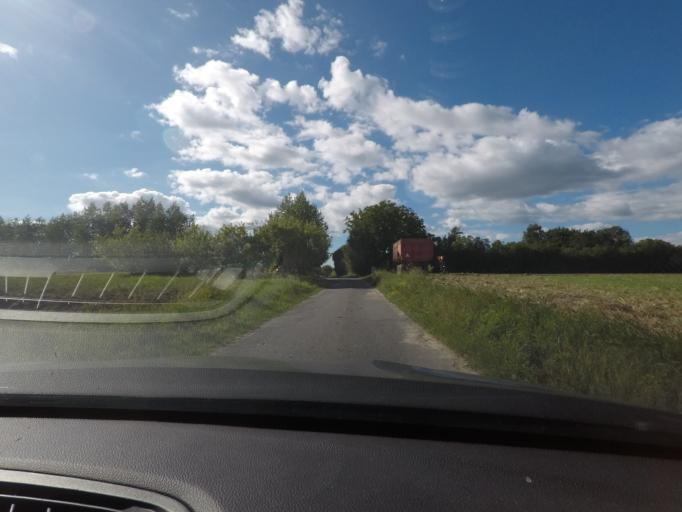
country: DK
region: Zealand
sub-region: Guldborgsund Kommune
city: Sakskobing
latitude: 54.9702
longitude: 11.5390
